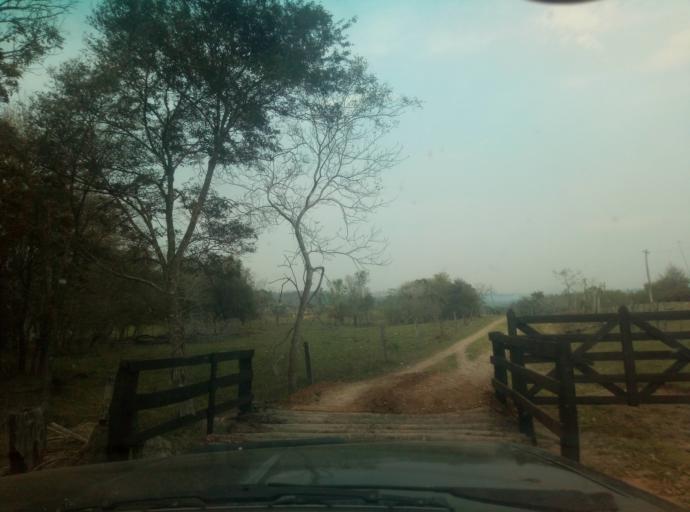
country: PY
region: Caaguazu
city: San Joaquin
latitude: -25.1045
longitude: -56.1280
